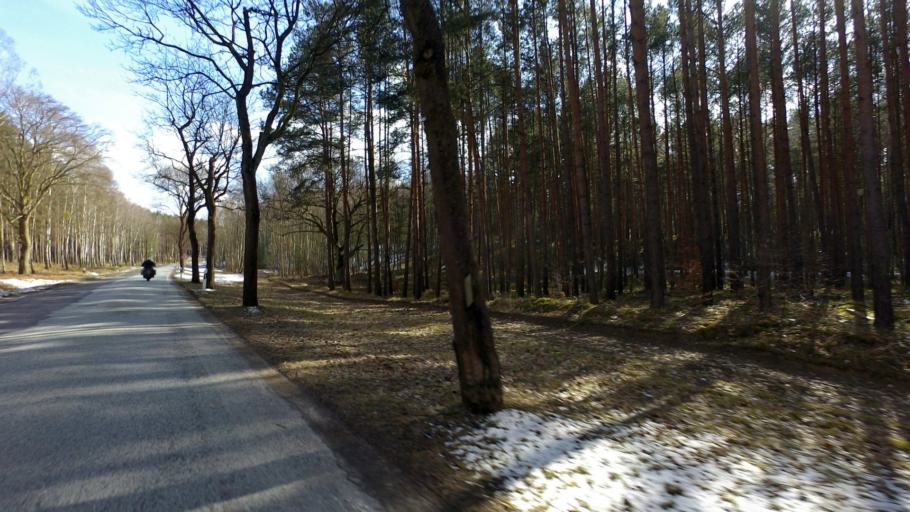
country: DE
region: Brandenburg
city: Biesenthal
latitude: 52.7925
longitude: 13.6027
